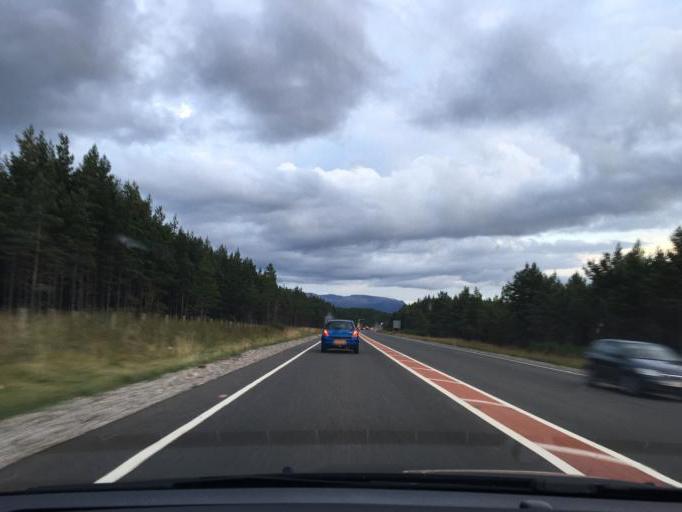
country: GB
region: Scotland
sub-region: Highland
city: Aviemore
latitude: 57.2702
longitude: -3.8175
